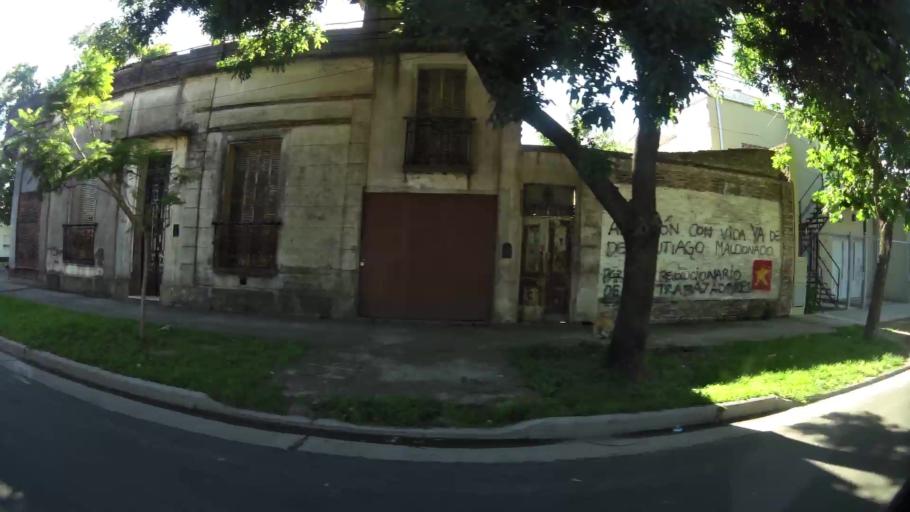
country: AR
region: Santa Fe
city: Santa Fe de la Vera Cruz
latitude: -31.6357
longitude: -60.6871
